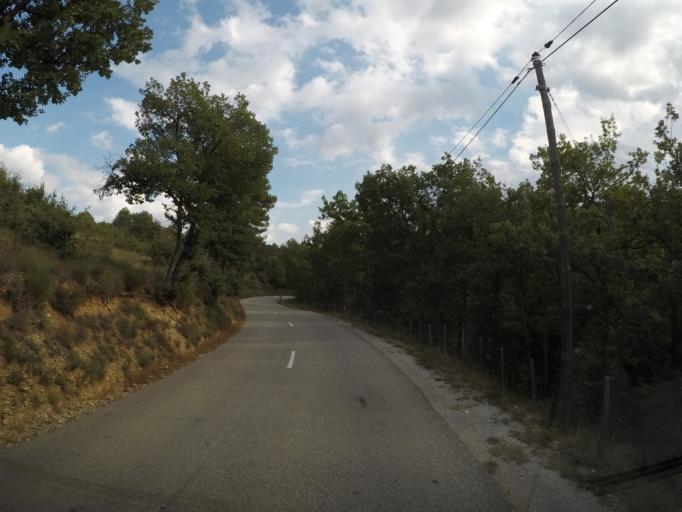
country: FR
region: Provence-Alpes-Cote d'Azur
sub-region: Departement des Alpes-de-Haute-Provence
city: Riez
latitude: 43.8265
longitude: 6.0427
